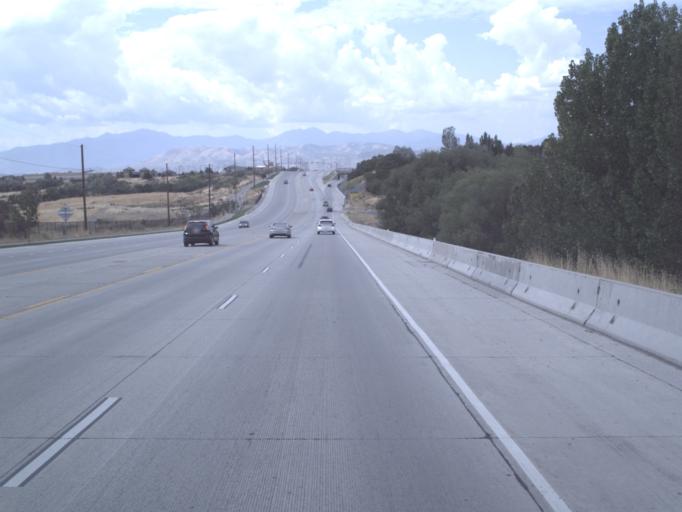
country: US
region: Utah
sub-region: Utah County
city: Alpine
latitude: 40.4319
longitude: -111.8135
